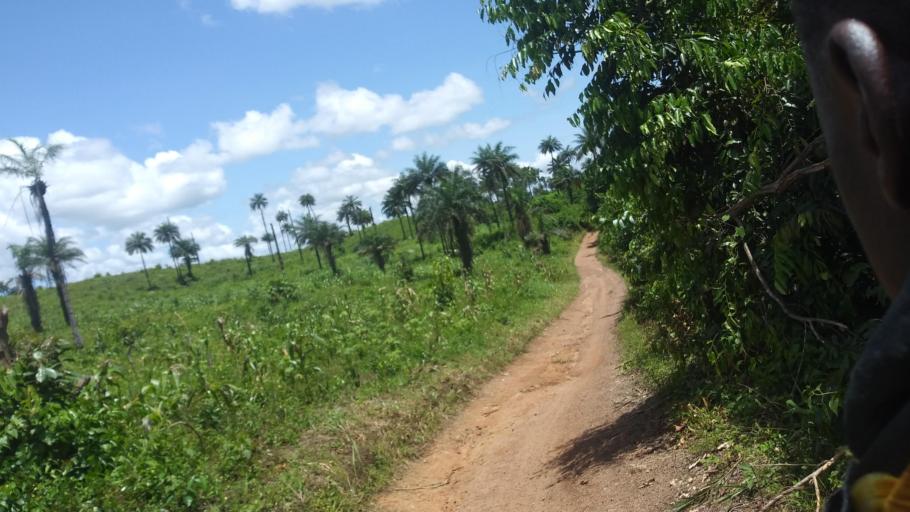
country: SL
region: Northern Province
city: Makeni
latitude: 8.8951
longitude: -12.0020
